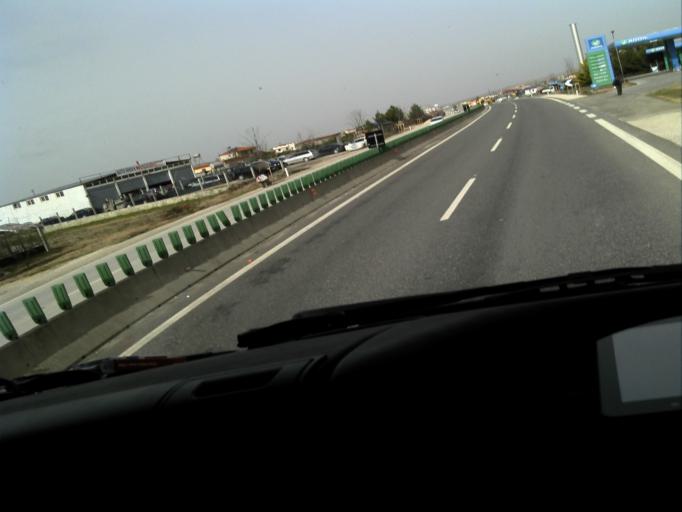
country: AL
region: Tirane
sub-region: Rrethi i Kavajes
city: Rrogozhine
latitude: 41.0417
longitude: 19.6570
